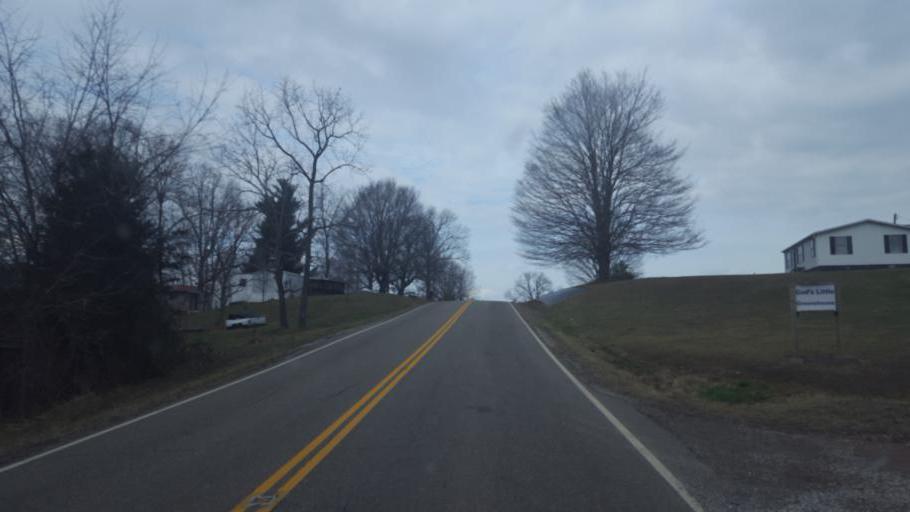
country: US
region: Ohio
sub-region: Jackson County
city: Oak Hill
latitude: 38.8094
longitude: -82.4005
